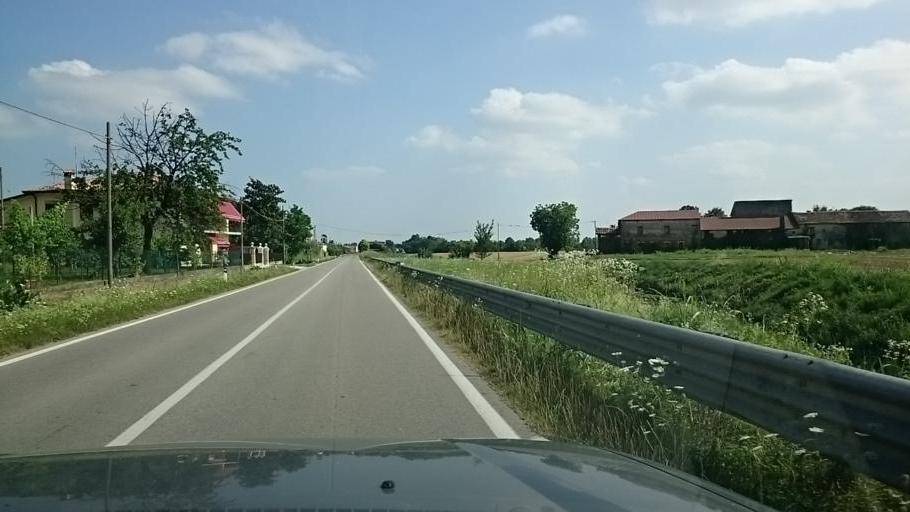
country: IT
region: Veneto
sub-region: Provincia di Padova
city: Villa del Conte
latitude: 45.5718
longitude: 11.8636
